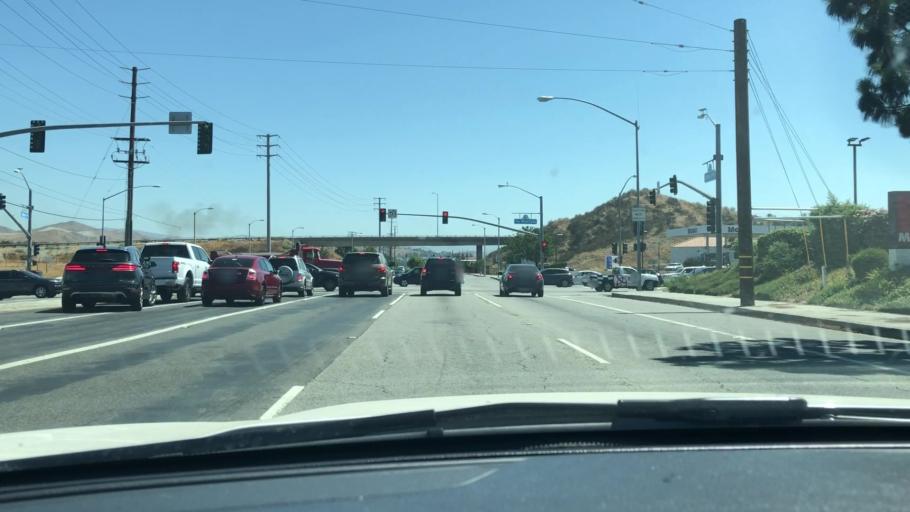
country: US
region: California
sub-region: Los Angeles County
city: Santa Clarita
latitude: 34.4052
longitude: -118.4653
